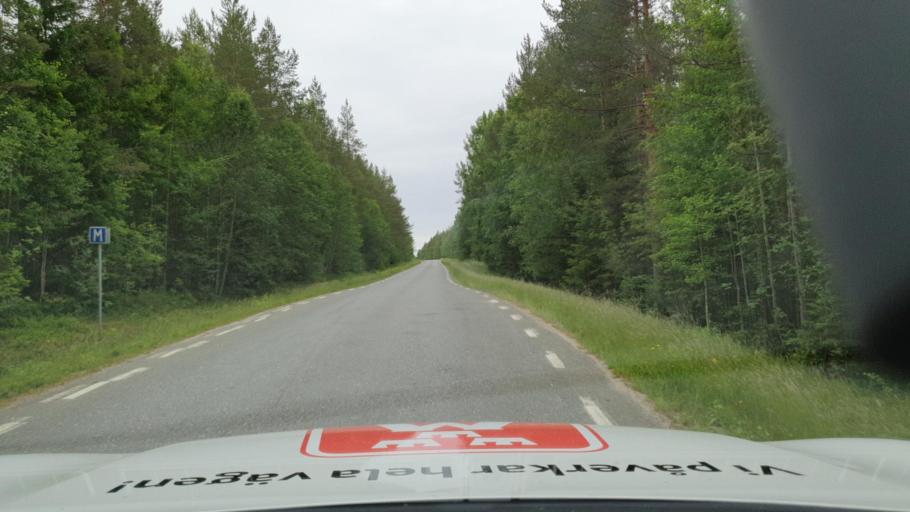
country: SE
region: Vaesterbotten
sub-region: Nordmalings Kommun
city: Nordmaling
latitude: 63.4788
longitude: 19.4584
